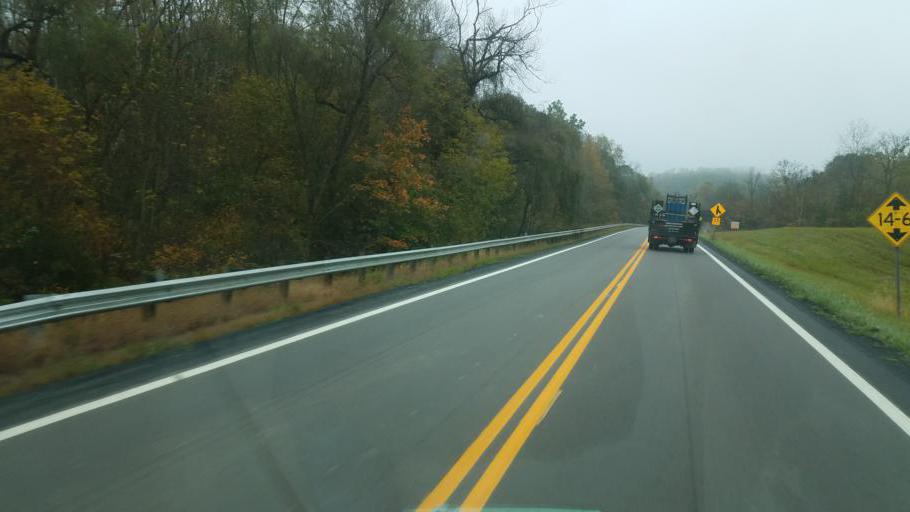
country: US
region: Ohio
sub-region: Tuscarawas County
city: Rockford
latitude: 40.4107
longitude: -81.2254
